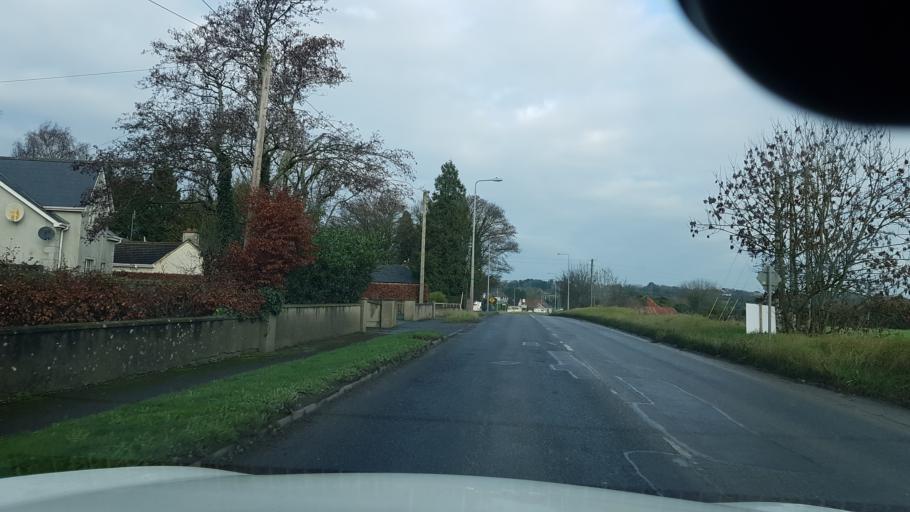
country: IE
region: Leinster
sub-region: An Mhi
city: Navan
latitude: 53.6690
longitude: -6.6801
